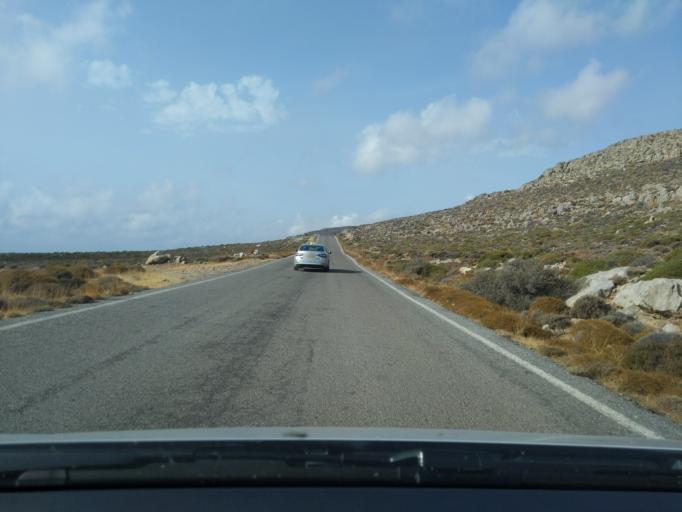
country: GR
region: Crete
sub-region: Nomos Lasithiou
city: Palekastro
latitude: 35.0860
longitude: 26.2647
